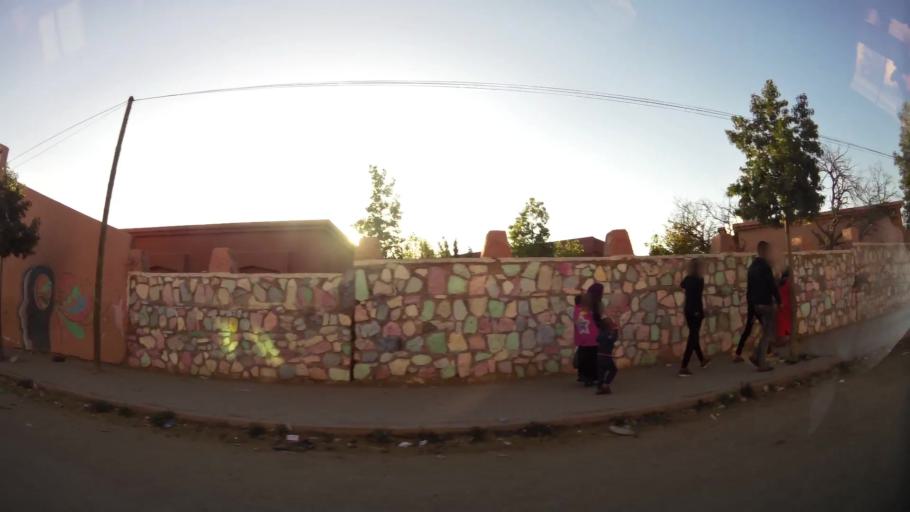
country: MA
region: Marrakech-Tensift-Al Haouz
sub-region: Kelaa-Des-Sraghna
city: Sidi Abdallah
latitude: 32.2465
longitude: -7.9471
